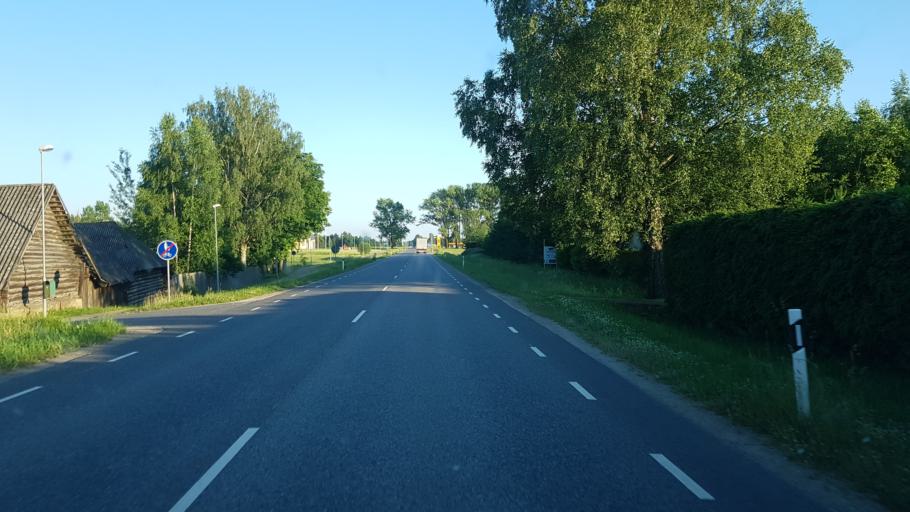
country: EE
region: Polvamaa
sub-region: Polva linn
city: Polva
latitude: 58.0671
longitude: 27.0486
